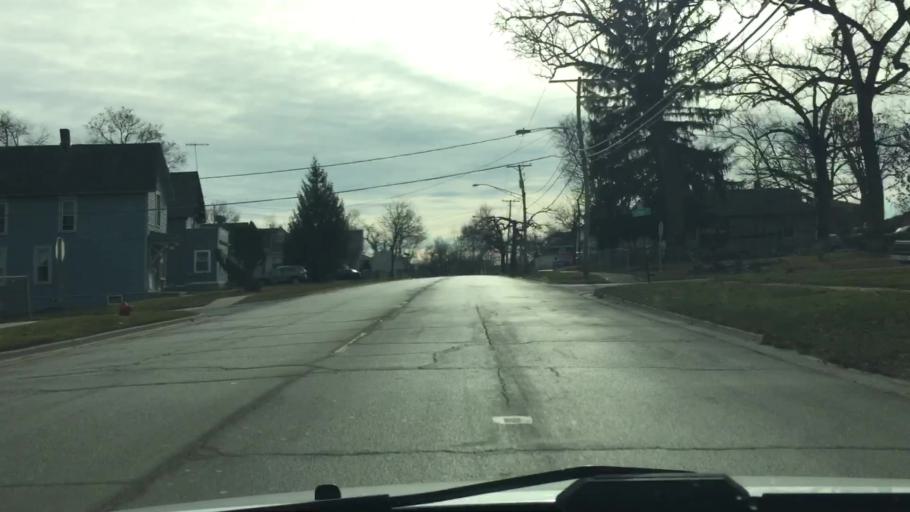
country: US
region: Illinois
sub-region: Kane County
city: Elgin
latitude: 42.0169
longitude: -88.2686
